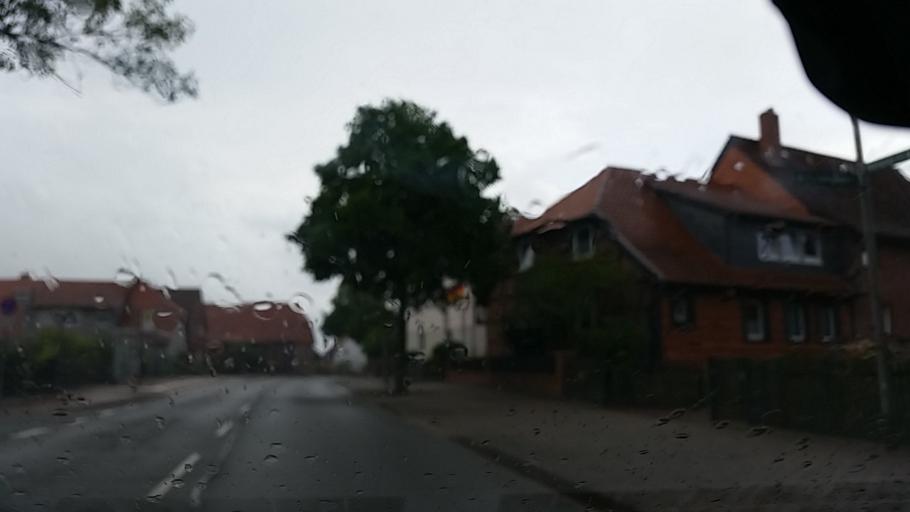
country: DE
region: Lower Saxony
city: Wolfsburg
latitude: 52.3605
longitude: 10.7504
